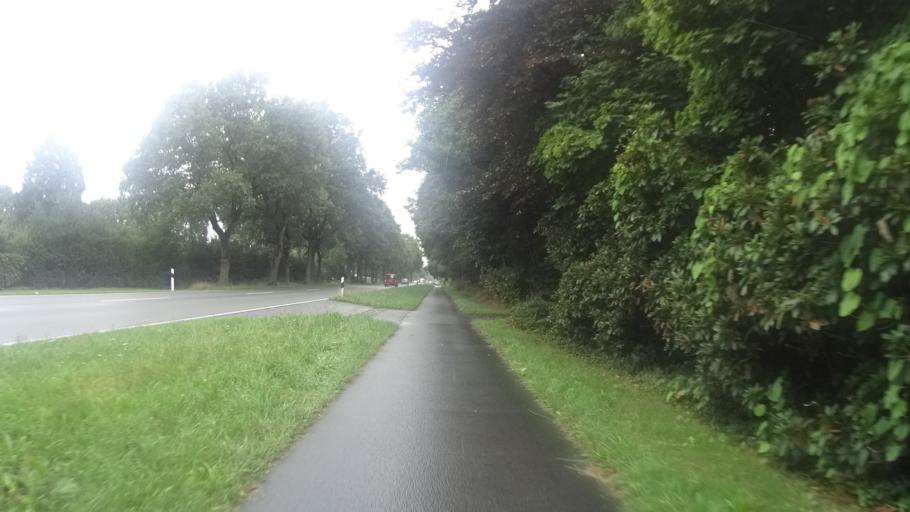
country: DE
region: Lower Saxony
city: Holtland
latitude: 53.2889
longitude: 7.5832
